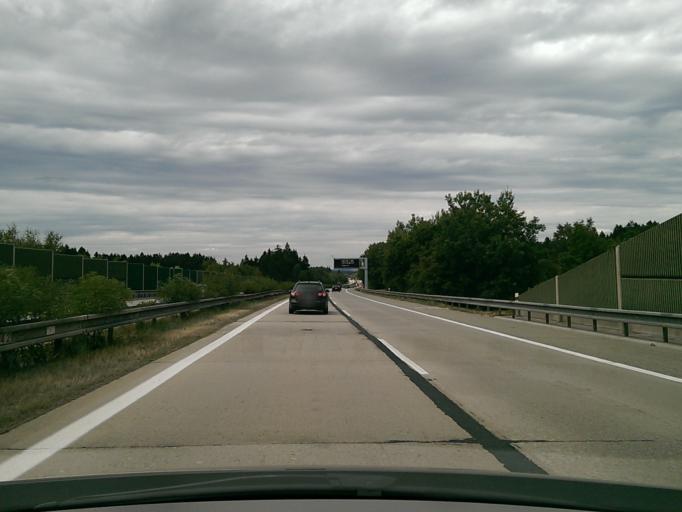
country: CZ
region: Vysocina
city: Kamenice
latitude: 49.4090
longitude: 15.7526
